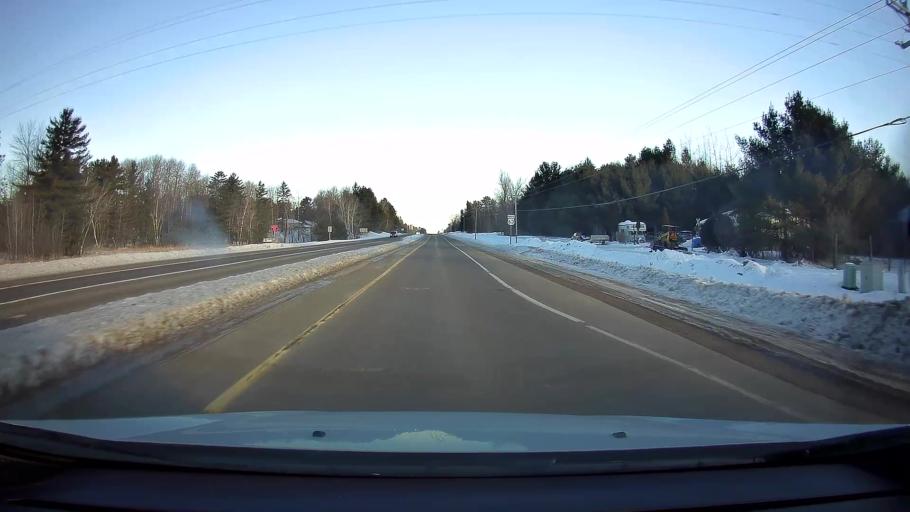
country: US
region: Wisconsin
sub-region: Barron County
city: Cumberland
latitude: 45.5587
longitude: -92.0172
